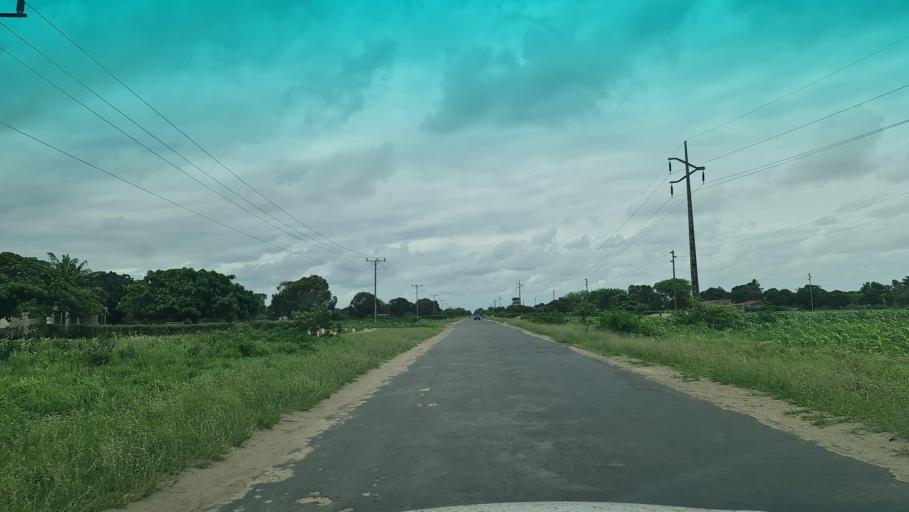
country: MZ
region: Maputo
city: Manhica
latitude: -25.4308
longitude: 32.7730
